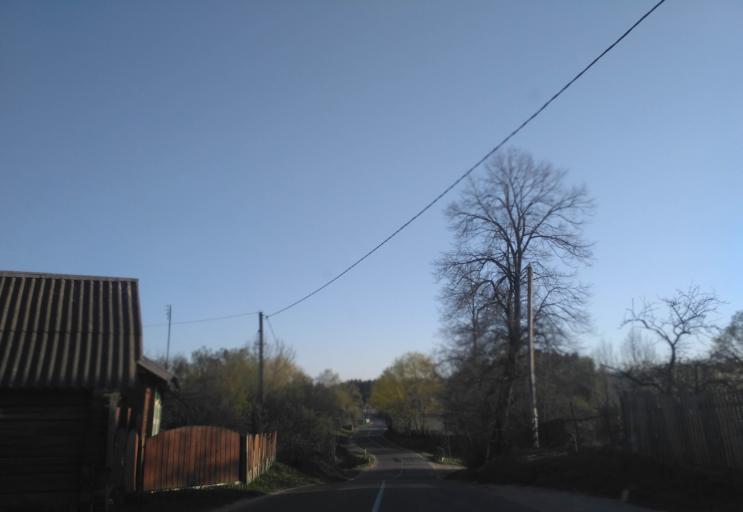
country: BY
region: Minsk
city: Radashkovichy
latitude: 54.1348
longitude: 27.2043
